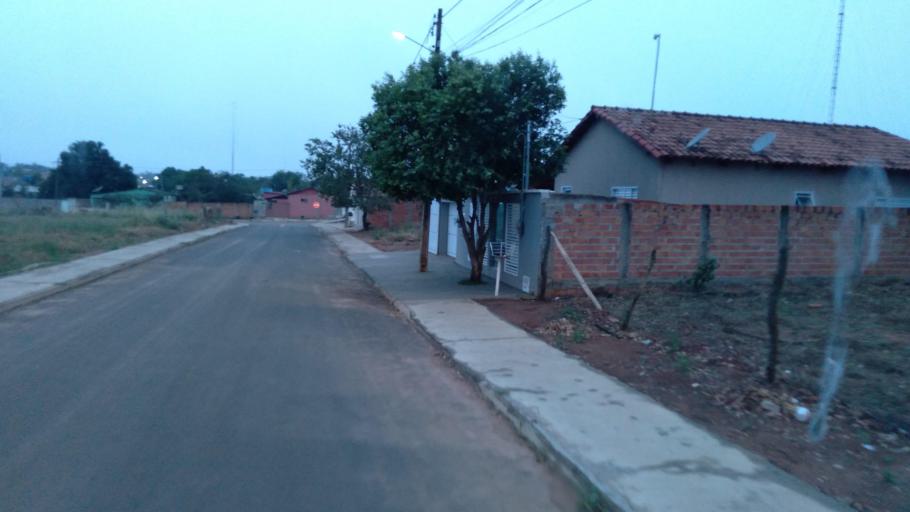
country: BR
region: Goias
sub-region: Mineiros
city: Mineiros
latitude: -17.5797
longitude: -52.5432
